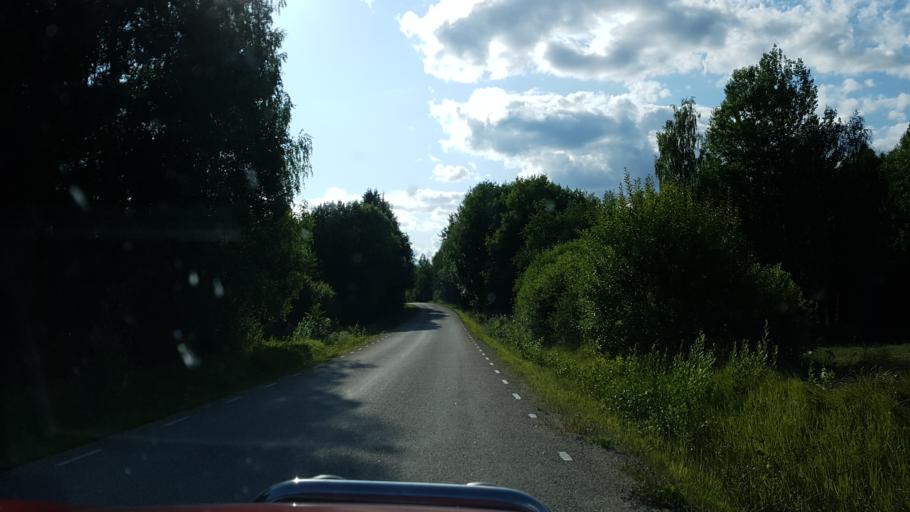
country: EE
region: Vorumaa
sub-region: Voru linn
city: Voru
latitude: 57.9282
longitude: 27.0574
